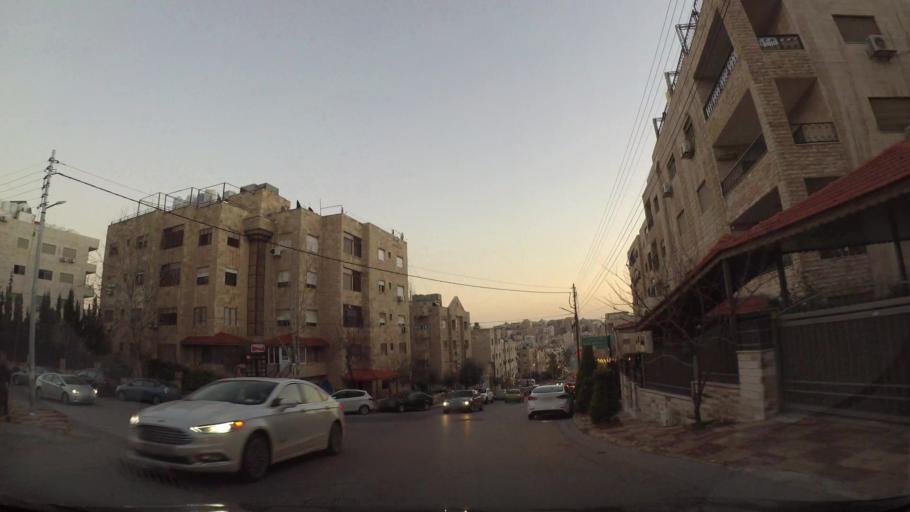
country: JO
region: Amman
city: Al Jubayhah
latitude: 31.9908
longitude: 35.8855
